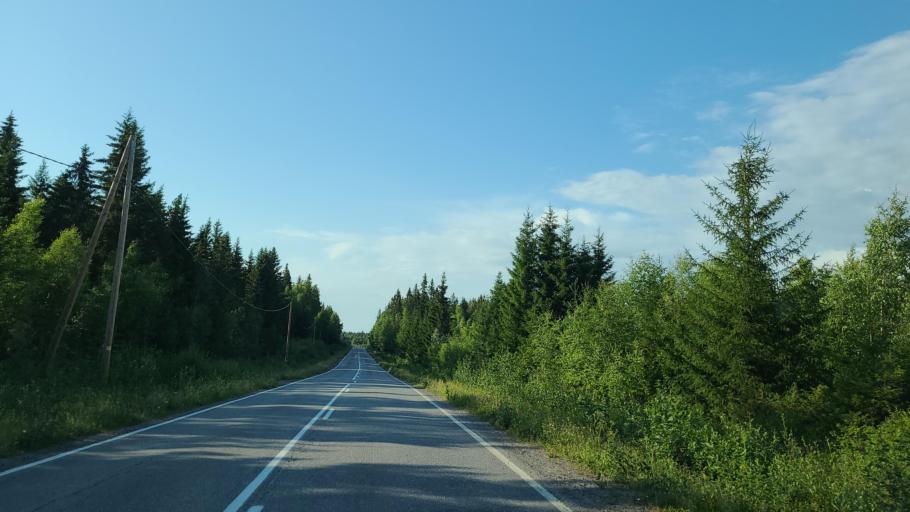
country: FI
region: Ostrobothnia
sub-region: Vaasa
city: Replot
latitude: 63.3133
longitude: 21.3596
